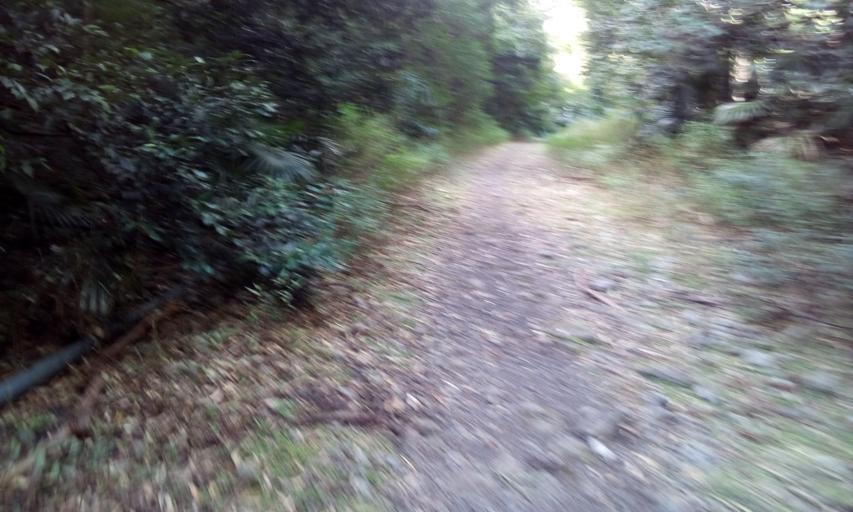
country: AU
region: New South Wales
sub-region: Wollongong
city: Cordeaux Heights
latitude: -34.4455
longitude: 150.8065
